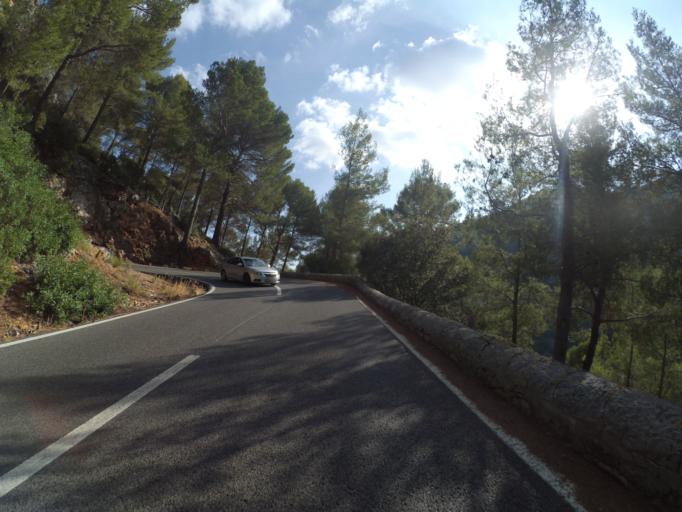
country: ES
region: Balearic Islands
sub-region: Illes Balears
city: Selva
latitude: 39.7775
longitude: 2.8986
